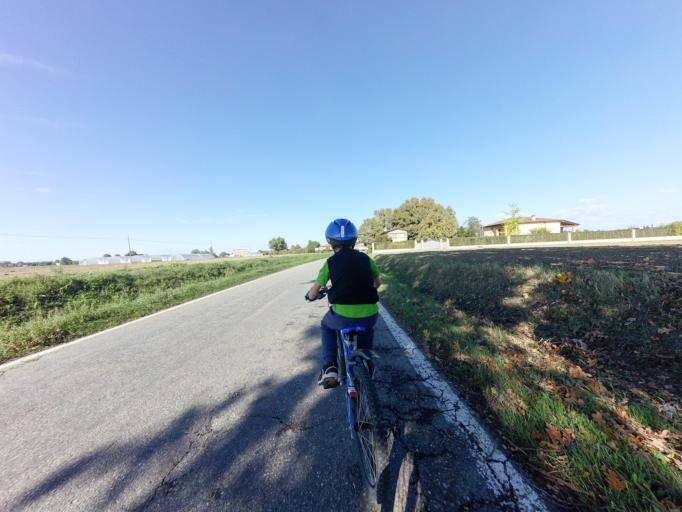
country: IT
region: Emilia-Romagna
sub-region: Provincia di Bologna
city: Bentivoglio
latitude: 44.5921
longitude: 11.4106
